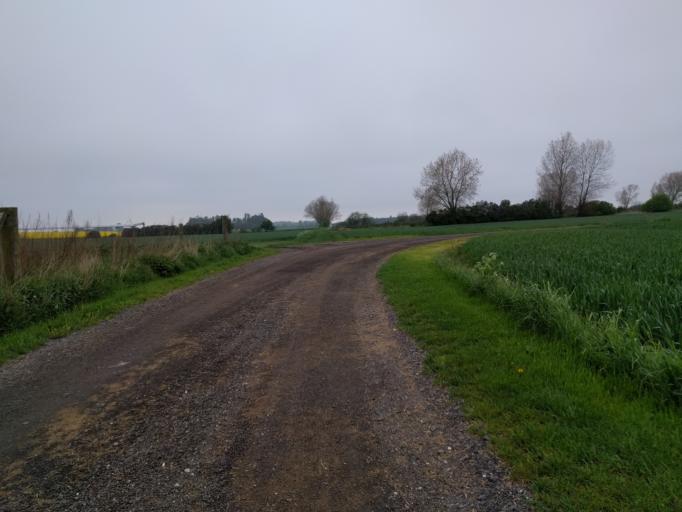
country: DK
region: South Denmark
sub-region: Kerteminde Kommune
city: Langeskov
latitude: 55.3962
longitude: 10.5330
